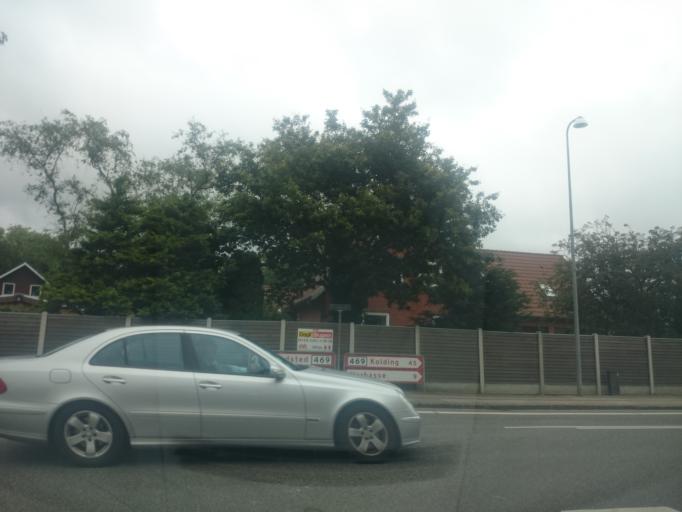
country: DK
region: South Denmark
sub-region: Billund Kommune
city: Grindsted
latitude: 55.6960
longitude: 8.9955
